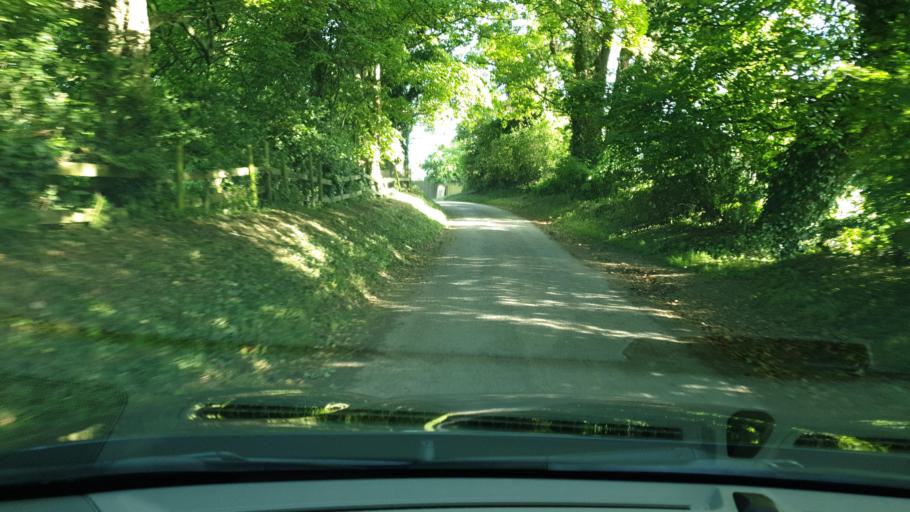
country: IE
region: Leinster
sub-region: An Mhi
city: Ashbourne
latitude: 53.5470
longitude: -6.4144
